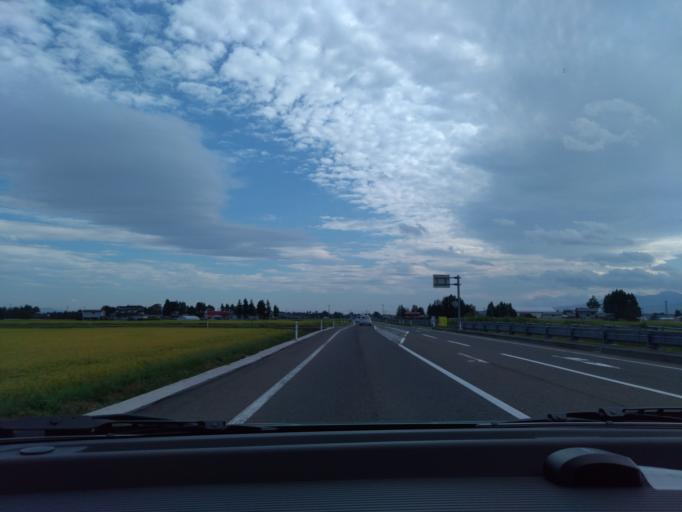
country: JP
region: Iwate
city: Hanamaki
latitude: 39.3687
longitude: 141.0568
